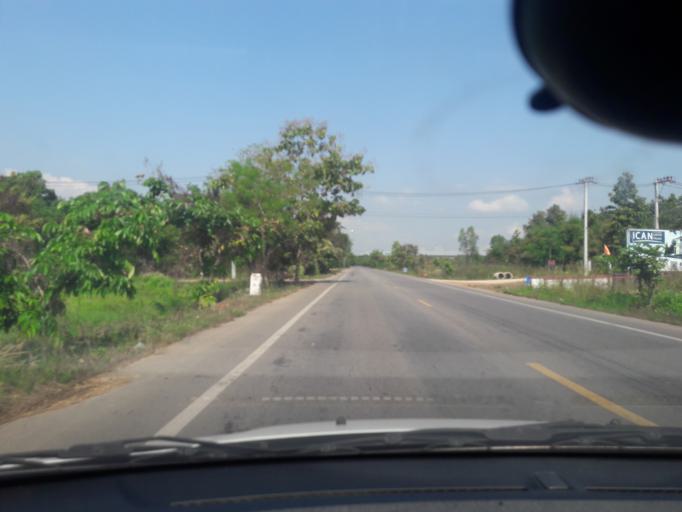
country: TH
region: Lampang
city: Lampang
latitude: 18.2173
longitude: 99.4923
